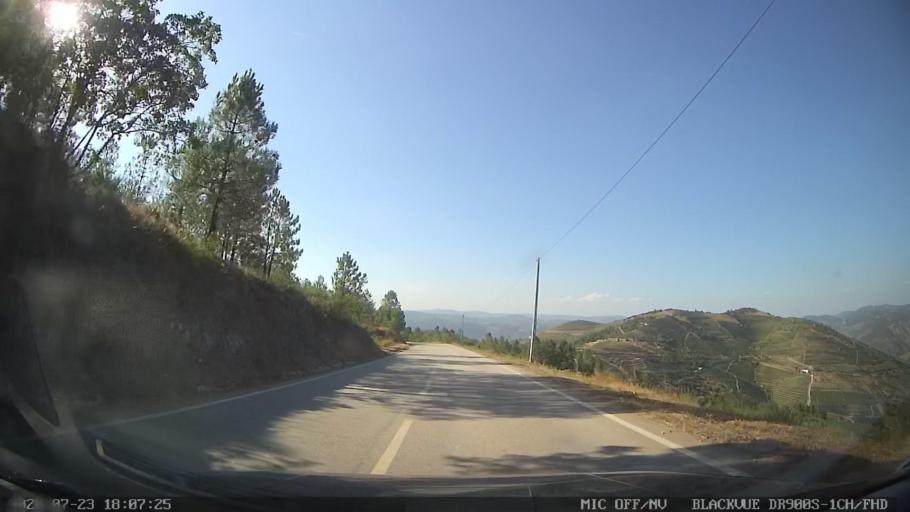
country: PT
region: Viseu
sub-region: Sao Joao da Pesqueira
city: Sao Joao da Pesqueira
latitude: 41.1679
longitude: -7.4359
